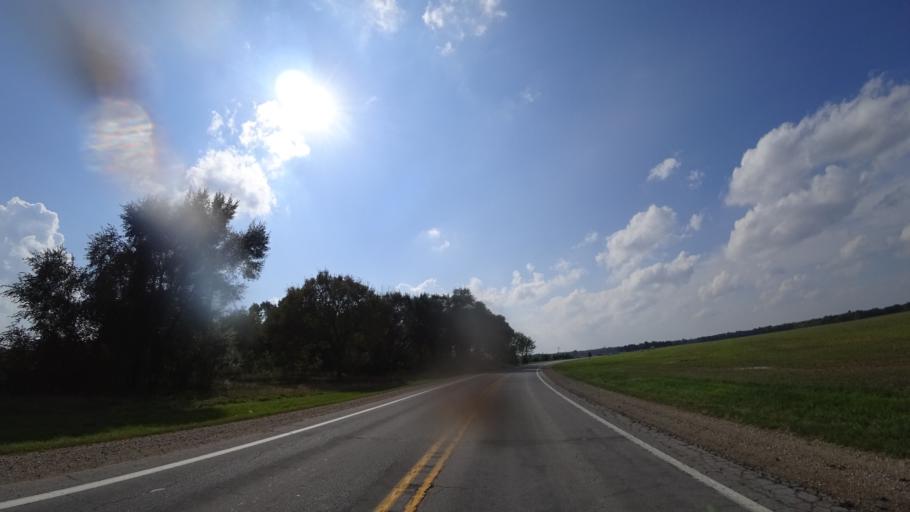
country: US
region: Michigan
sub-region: Saint Joseph County
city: Colon
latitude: 42.0112
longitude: -85.3651
